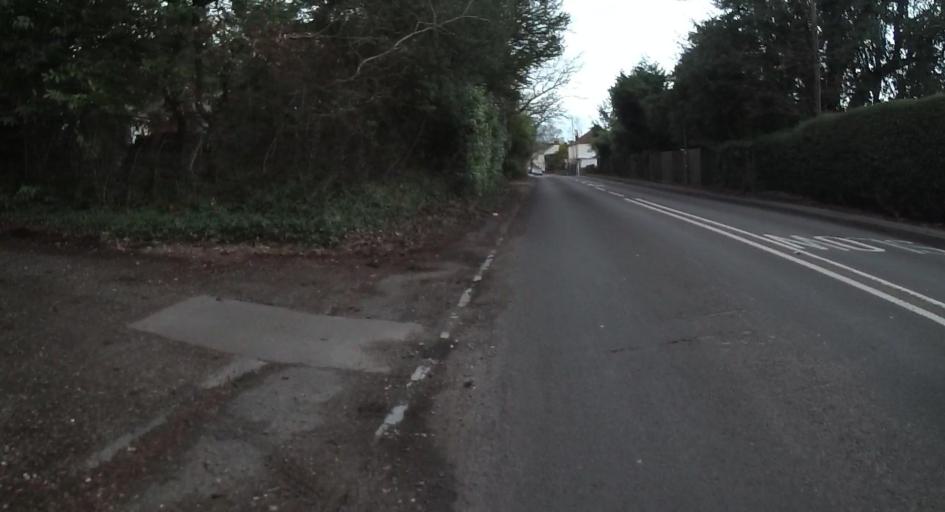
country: GB
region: England
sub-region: Surrey
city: Farnham
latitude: 51.1946
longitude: -0.7889
